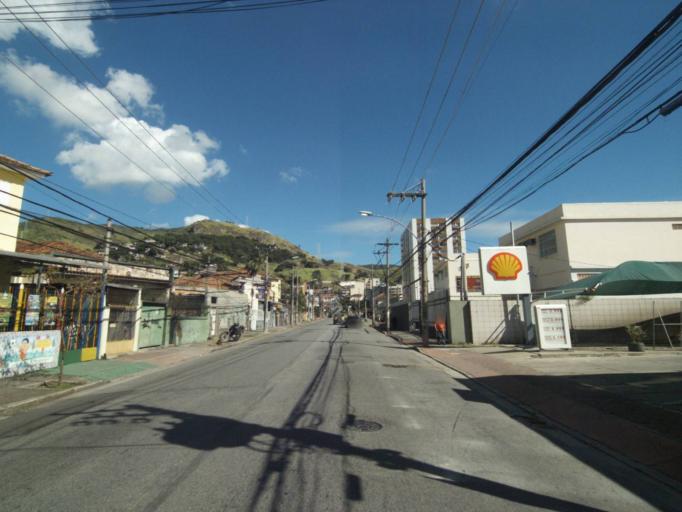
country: BR
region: Rio de Janeiro
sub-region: Rio De Janeiro
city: Rio de Janeiro
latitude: -22.9106
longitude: -43.2843
